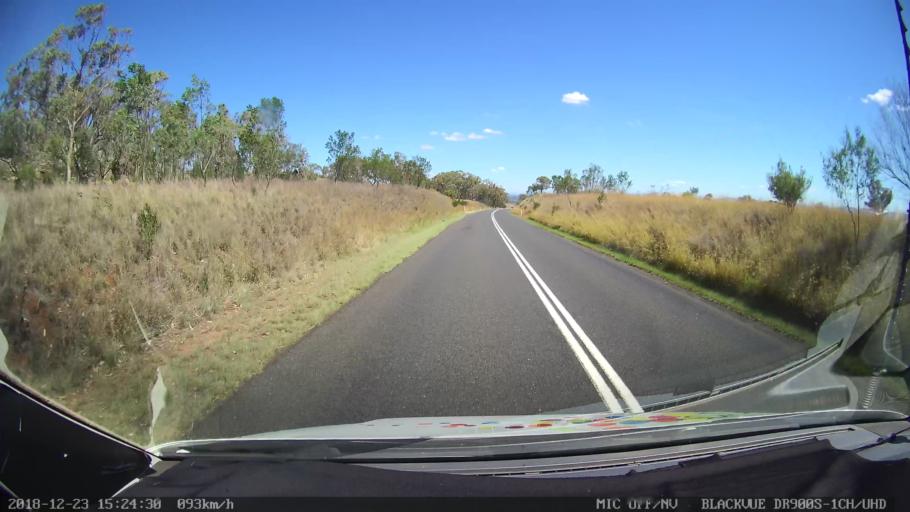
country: AU
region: New South Wales
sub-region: Tamworth Municipality
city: Manilla
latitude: -30.8925
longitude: 150.8237
